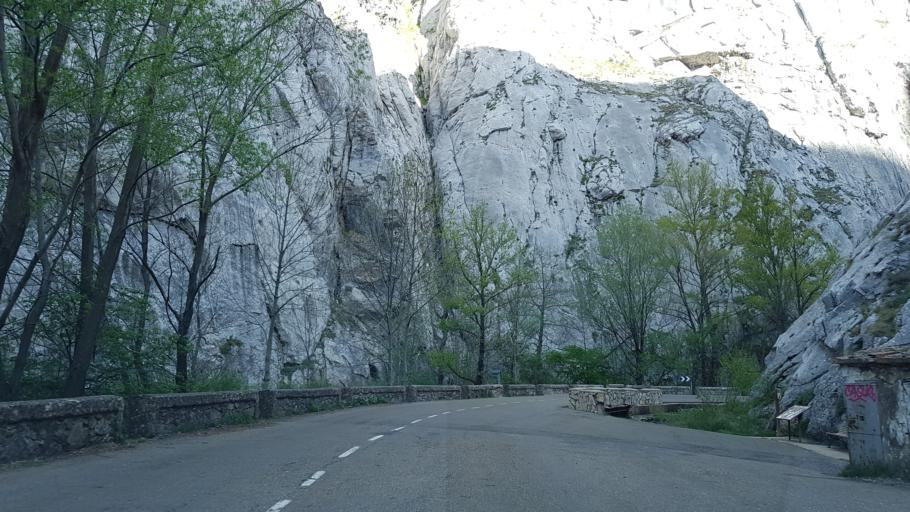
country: ES
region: Castille and Leon
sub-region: Provincia de Leon
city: Vegacervera
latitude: 42.9025
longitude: -5.5390
